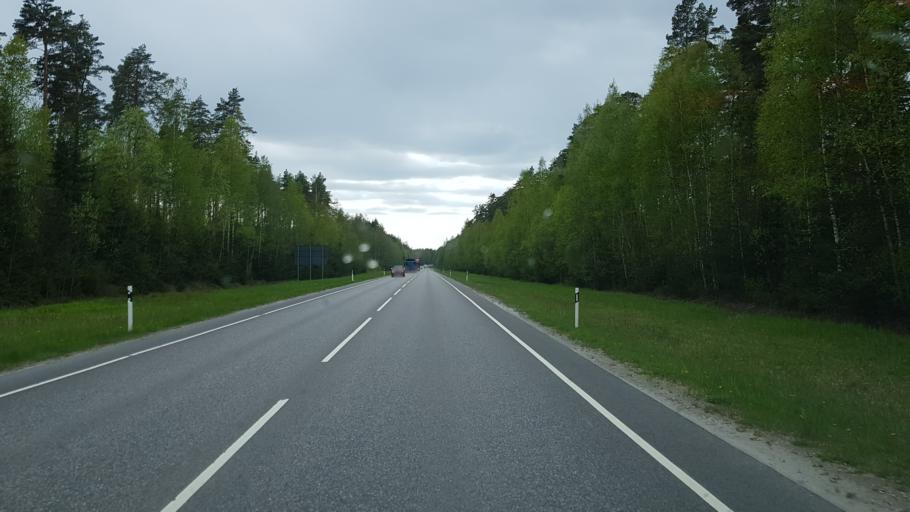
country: EE
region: Paernumaa
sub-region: Saarde vald
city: Kilingi-Nomme
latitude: 58.1544
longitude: 24.9269
